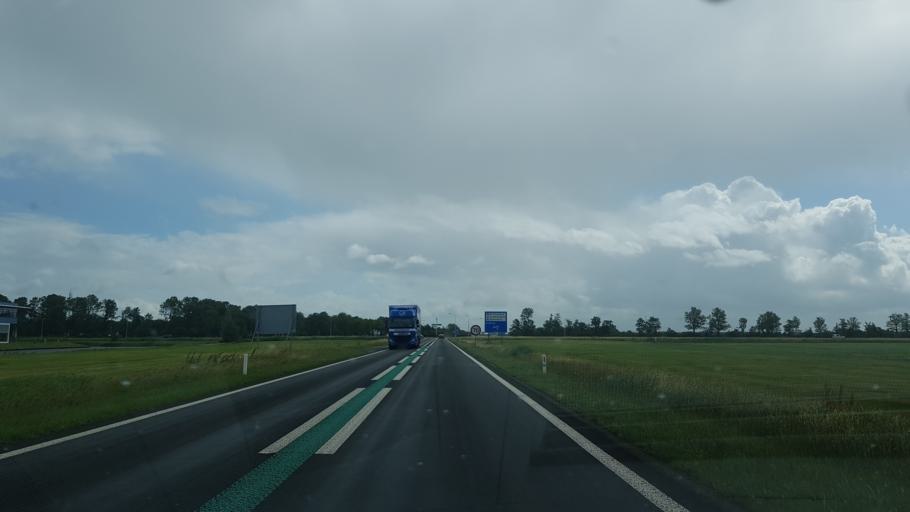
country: NL
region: Friesland
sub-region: Gemeente Dongeradeel
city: Dokkum
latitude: 53.3103
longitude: 5.9893
